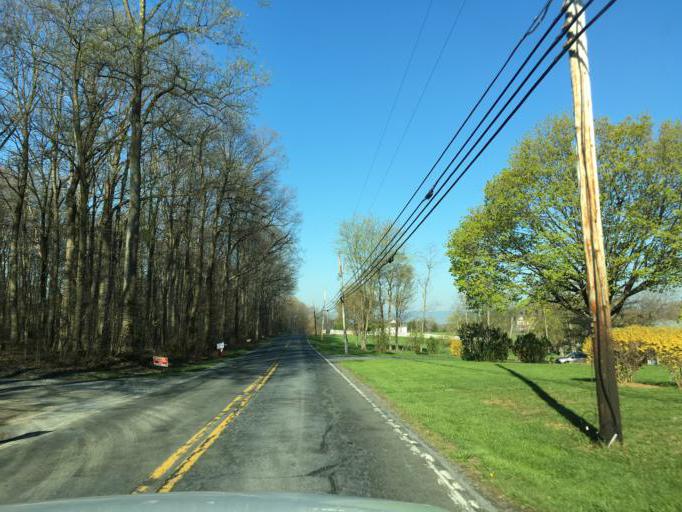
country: US
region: Maryland
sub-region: Frederick County
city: Woodsboro
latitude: 39.4866
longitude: -77.2683
